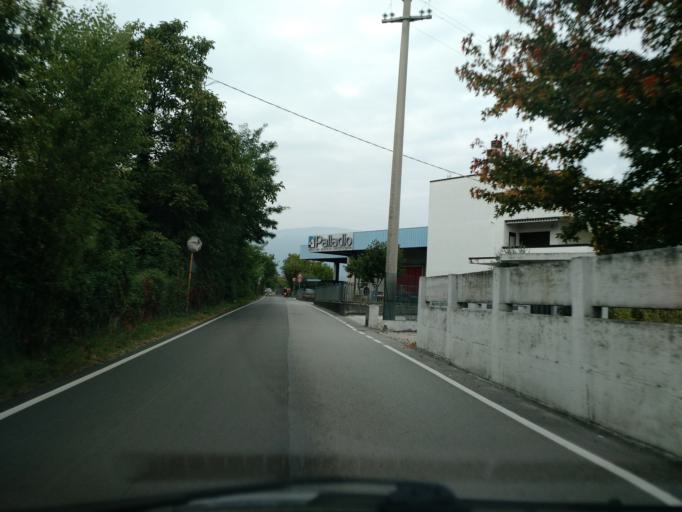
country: IT
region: Veneto
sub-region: Provincia di Vicenza
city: Thiene
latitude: 45.6891
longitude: 11.4752
